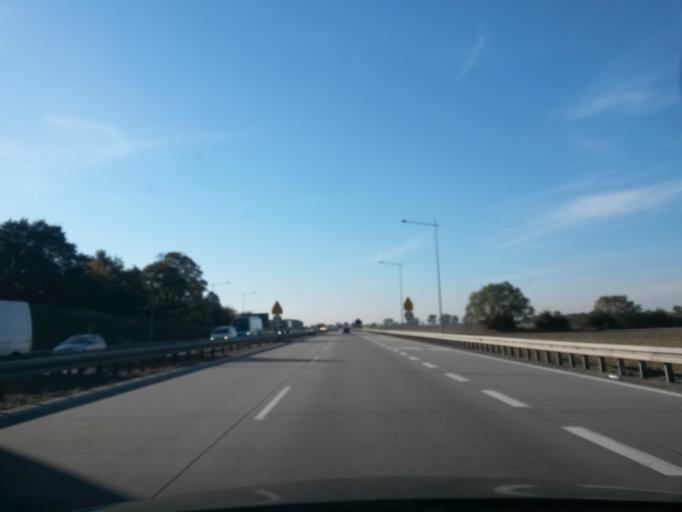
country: PL
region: Lower Silesian Voivodeship
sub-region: Powiat sredzki
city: Ciechow
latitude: 51.0432
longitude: 16.5940
